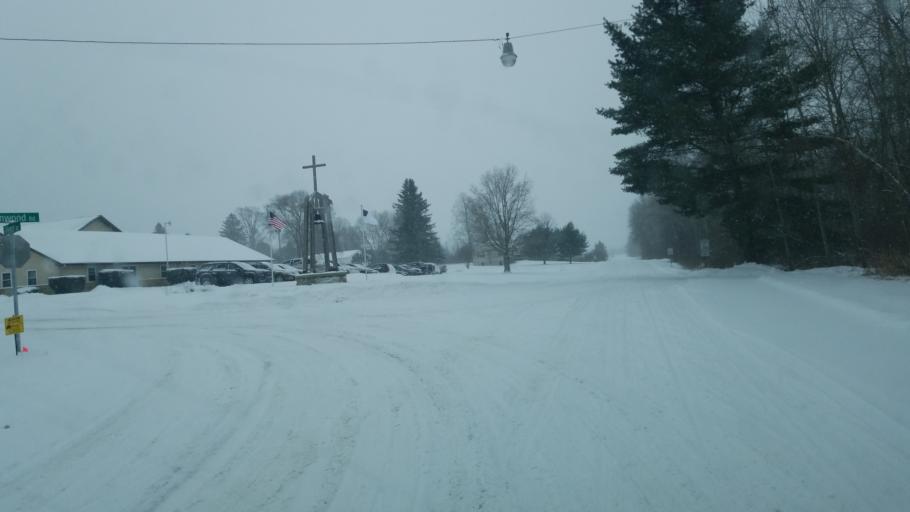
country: US
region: Michigan
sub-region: Mecosta County
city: Big Rapids
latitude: 43.5767
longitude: -85.4483
